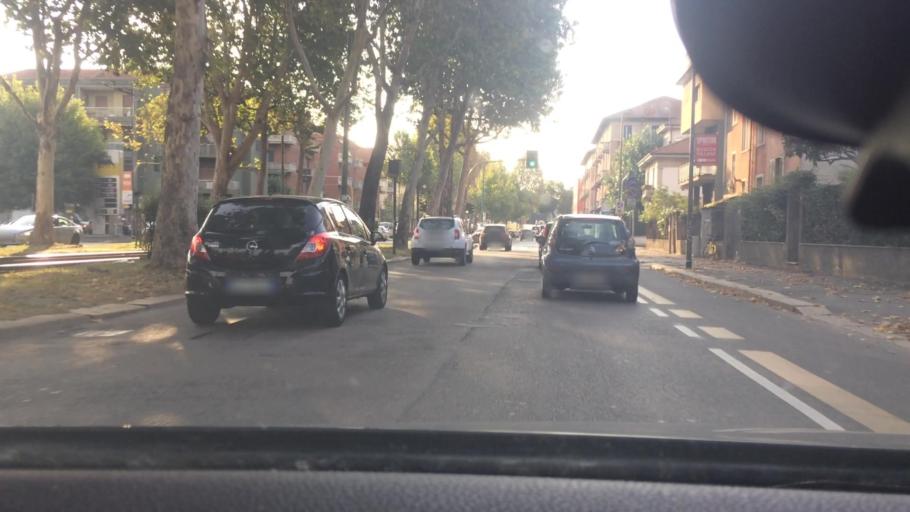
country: IT
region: Lombardy
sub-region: Citta metropolitana di Milano
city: Milano
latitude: 45.4953
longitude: 9.1952
